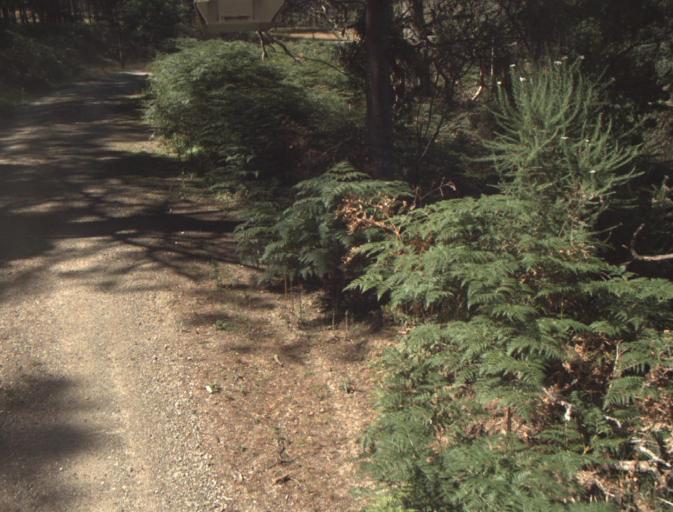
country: AU
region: Tasmania
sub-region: Dorset
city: Scottsdale
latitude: -41.2612
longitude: 147.3504
